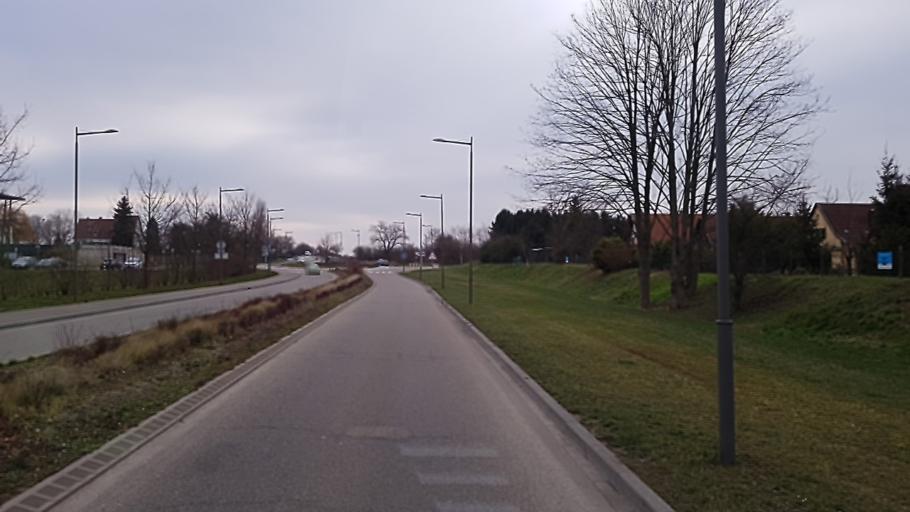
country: FR
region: Alsace
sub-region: Departement du Bas-Rhin
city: Niedernai
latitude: 48.4589
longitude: 7.5017
